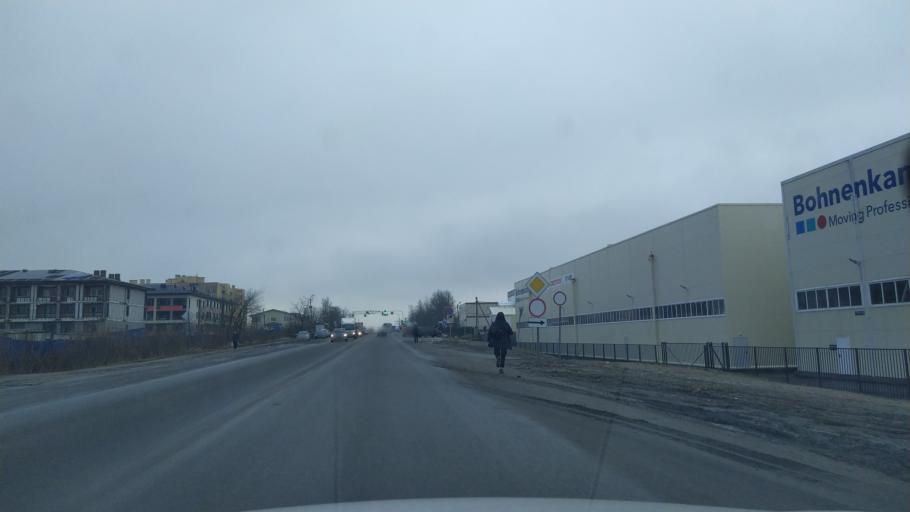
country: RU
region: St.-Petersburg
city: Aleksandrovskaya
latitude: 59.7226
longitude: 30.2628
